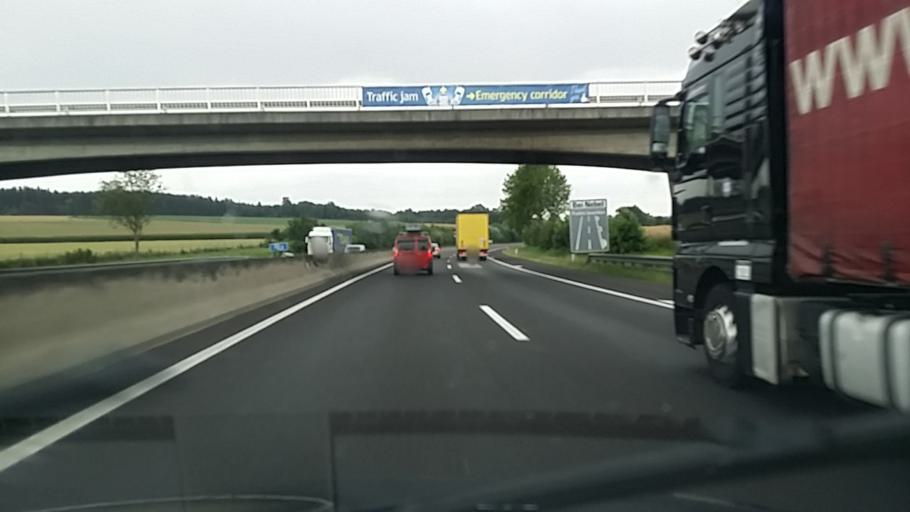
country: AT
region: Upper Austria
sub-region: Politischer Bezirk Scharding
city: Sankt Marienkirchen bei Schaerding
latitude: 48.3589
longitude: 13.4144
